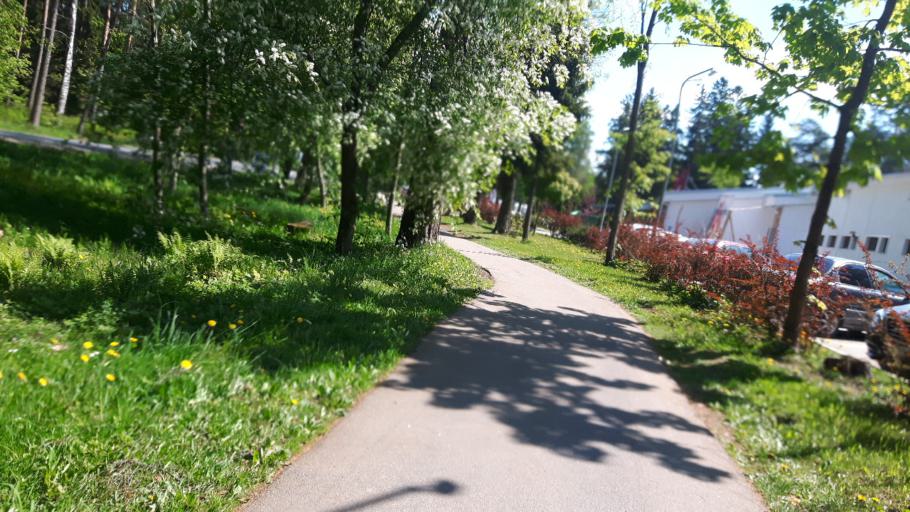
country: RU
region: St.-Petersburg
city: Komarovo
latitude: 60.1684
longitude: 29.8213
